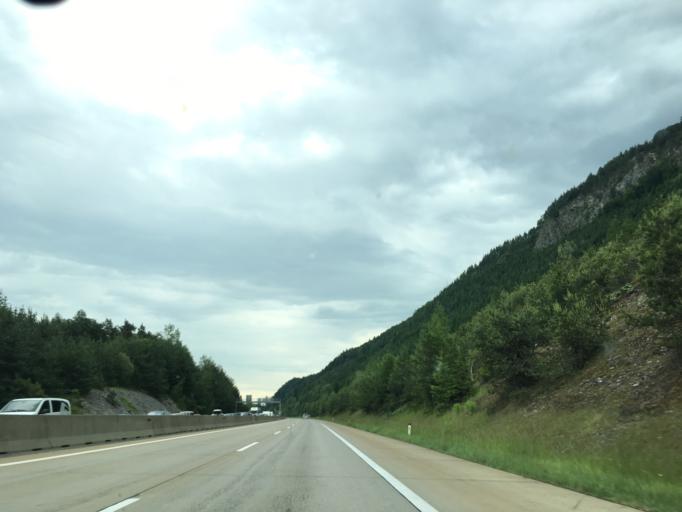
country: AT
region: Carinthia
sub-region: Politischer Bezirk Villach Land
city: Fresach
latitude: 46.6495
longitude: 13.7546
